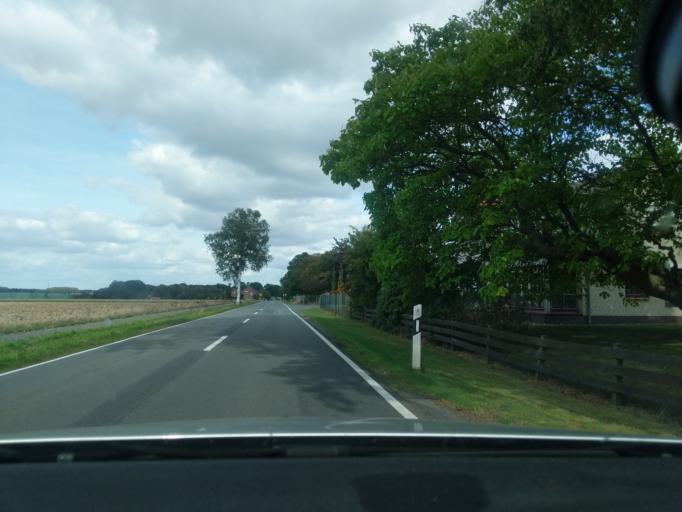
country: DE
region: Lower Saxony
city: Wietzen
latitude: 52.7399
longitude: 9.0641
